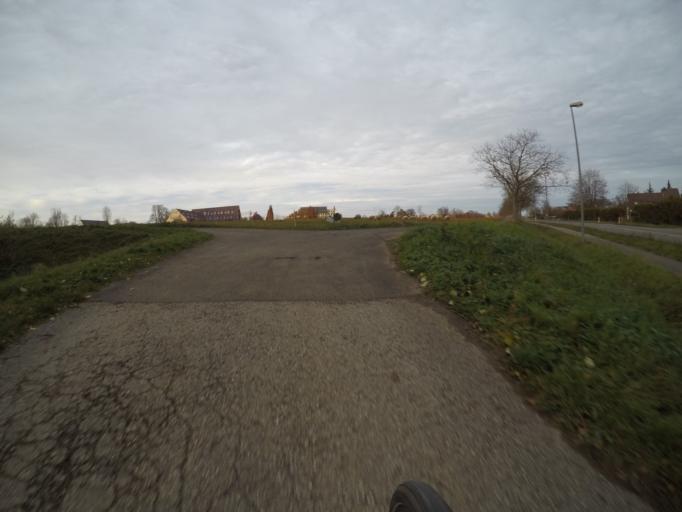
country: DE
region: Baden-Wuerttemberg
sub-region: Regierungsbezirk Stuttgart
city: Ostfildern
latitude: 48.7113
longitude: 9.2726
